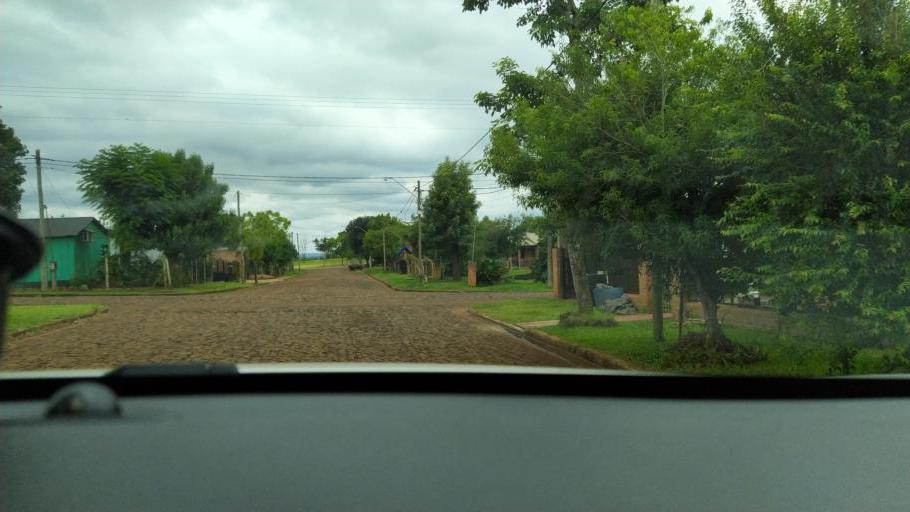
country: AR
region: Misiones
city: Garuhape
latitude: -26.8216
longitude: -54.9548
